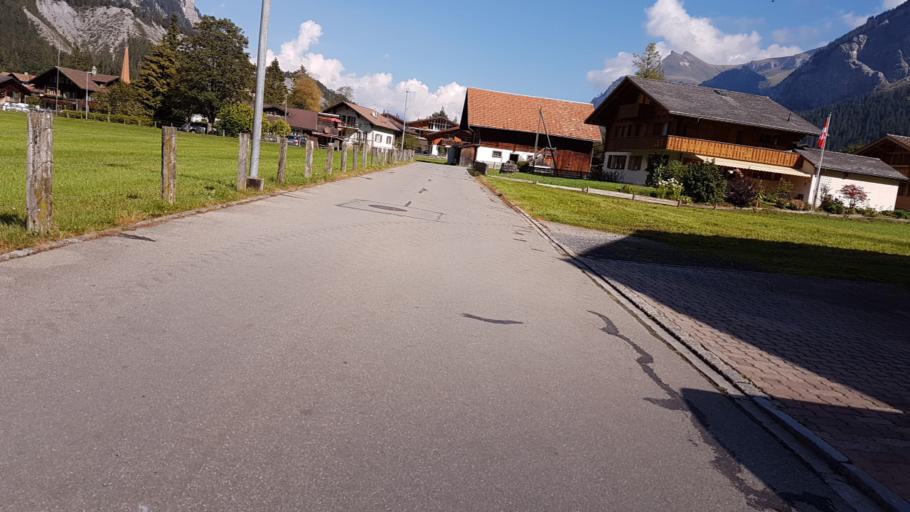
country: CH
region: Bern
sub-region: Frutigen-Niedersimmental District
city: Kandersteg
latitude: 46.4928
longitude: 7.6760
